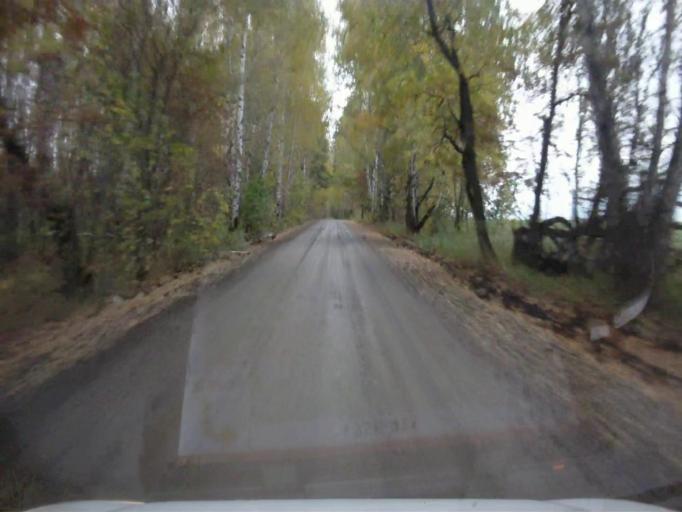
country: RU
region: Sverdlovsk
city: Mikhaylovsk
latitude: 56.1707
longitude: 59.2232
